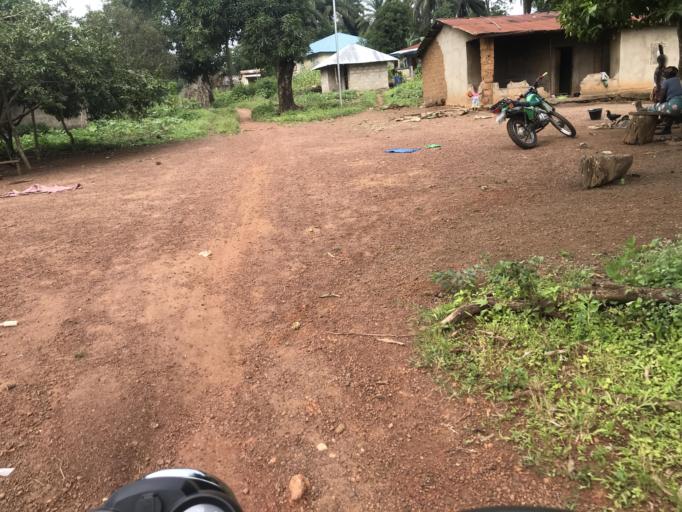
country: SL
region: Eastern Province
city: Buedu
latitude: 8.4677
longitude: -10.3336
